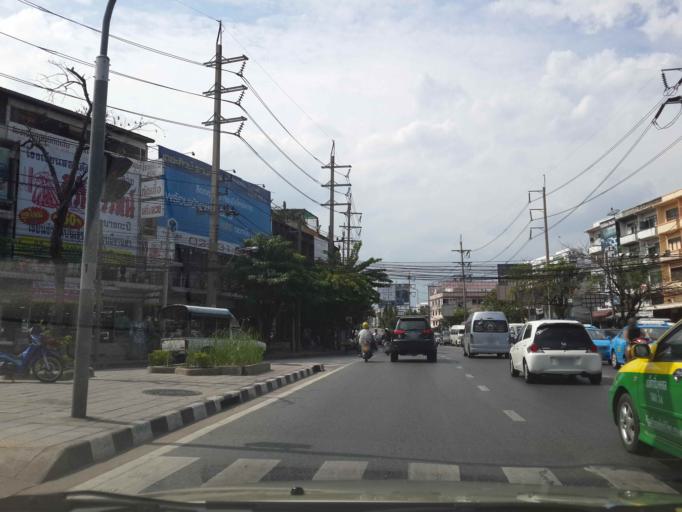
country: TH
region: Bangkok
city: Bang Kapi
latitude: 13.7627
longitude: 100.6455
